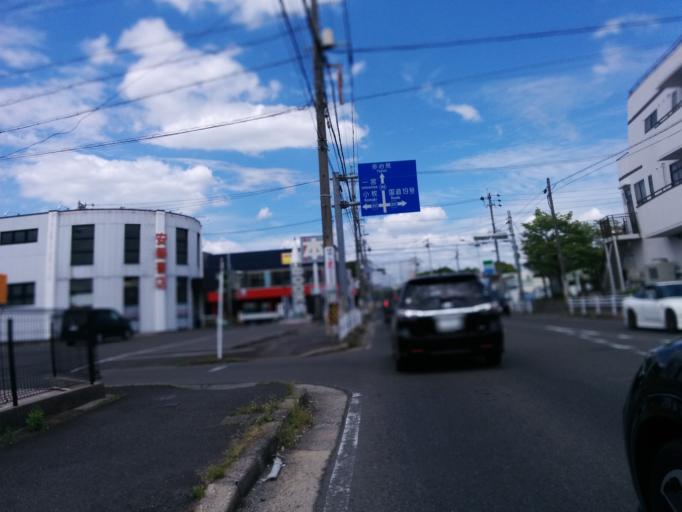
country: JP
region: Aichi
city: Kasugai
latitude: 35.2690
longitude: 136.9845
